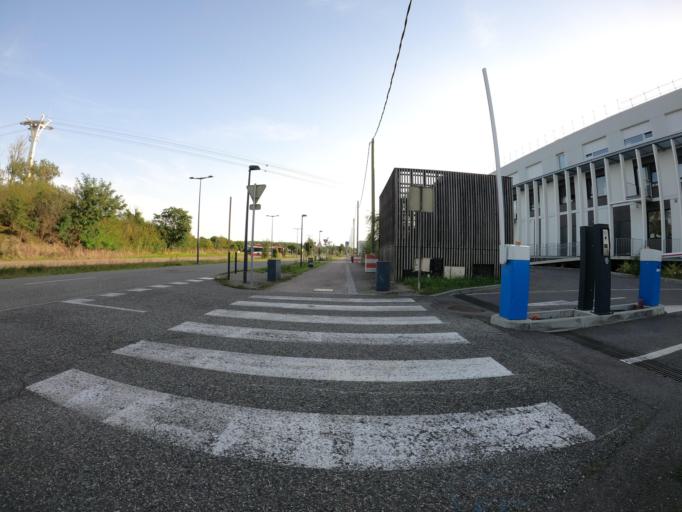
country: FR
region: Midi-Pyrenees
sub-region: Departement de la Haute-Garonne
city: Vieille-Toulouse
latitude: 43.5562
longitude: 1.4316
